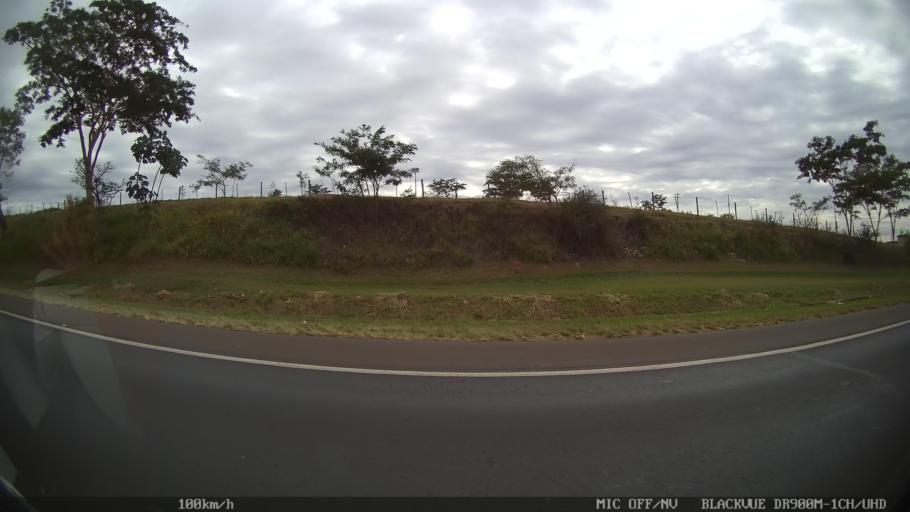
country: BR
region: Sao Paulo
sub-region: Sao Jose Do Rio Preto
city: Sao Jose do Rio Preto
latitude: -20.8145
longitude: -49.4695
